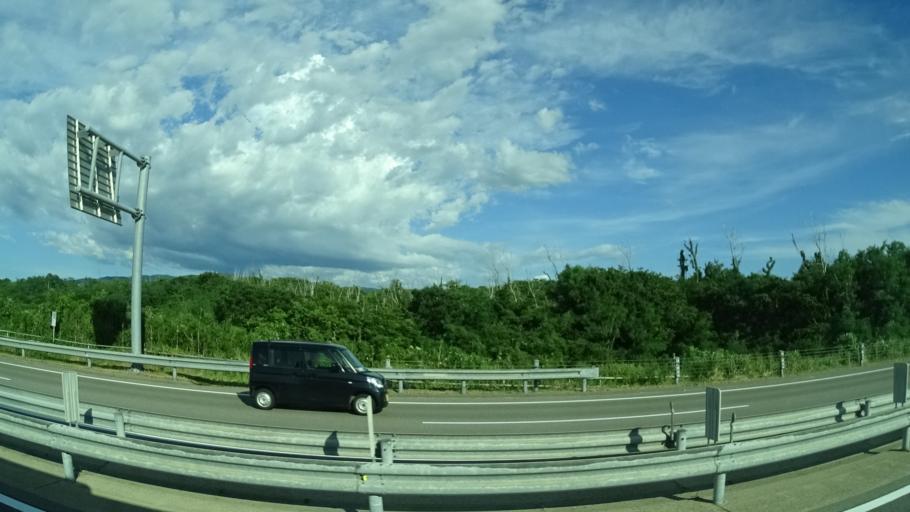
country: JP
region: Ishikawa
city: Hakui
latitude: 36.7937
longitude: 136.7295
